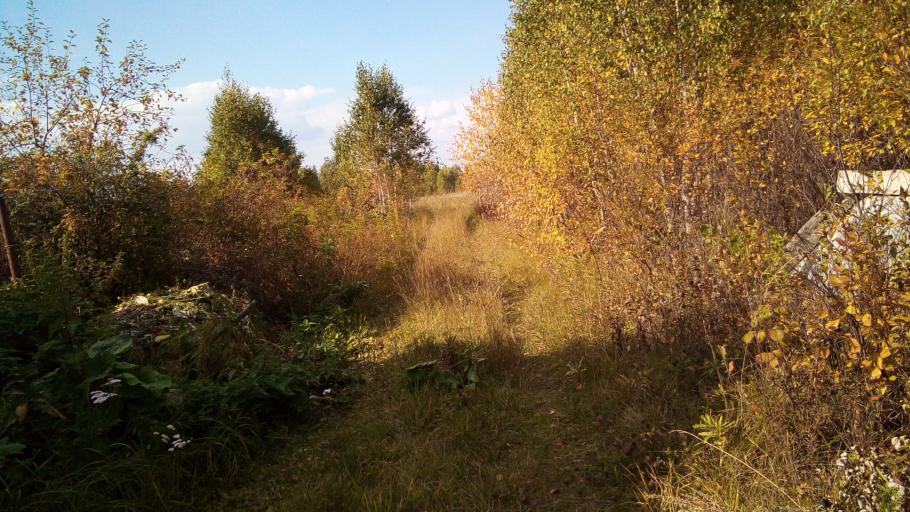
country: RU
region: Chelyabinsk
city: Timiryazevskiy
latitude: 54.9951
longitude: 60.8503
